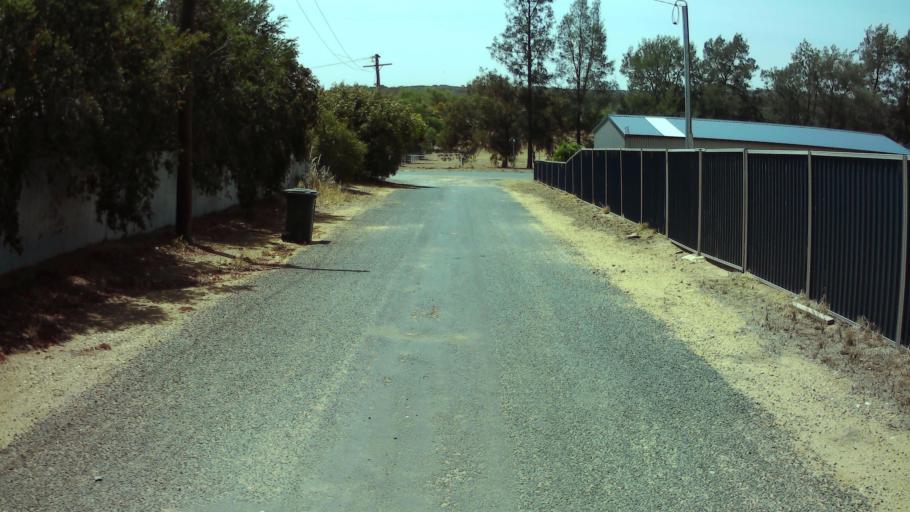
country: AU
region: New South Wales
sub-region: Weddin
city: Grenfell
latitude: -33.8941
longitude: 148.1702
